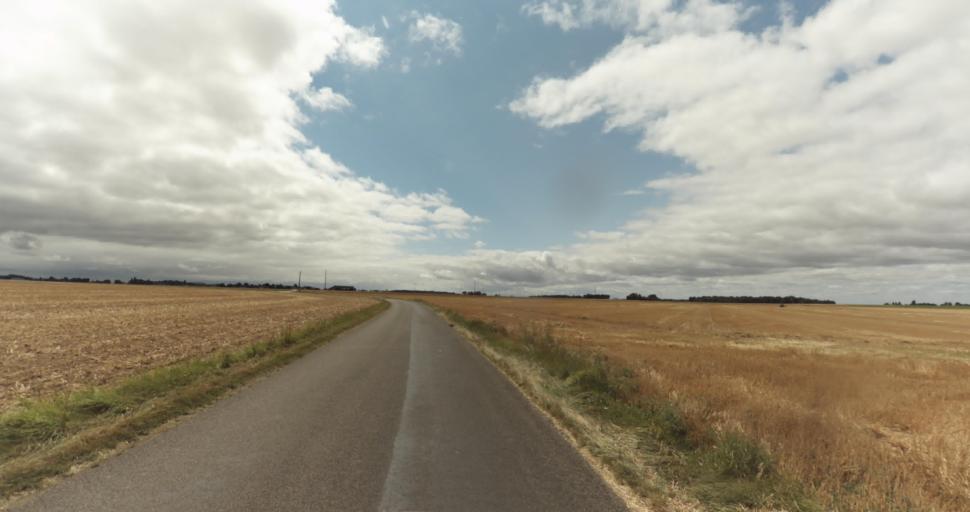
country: FR
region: Haute-Normandie
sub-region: Departement de l'Eure
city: Marcilly-sur-Eure
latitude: 48.9132
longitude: 1.2417
